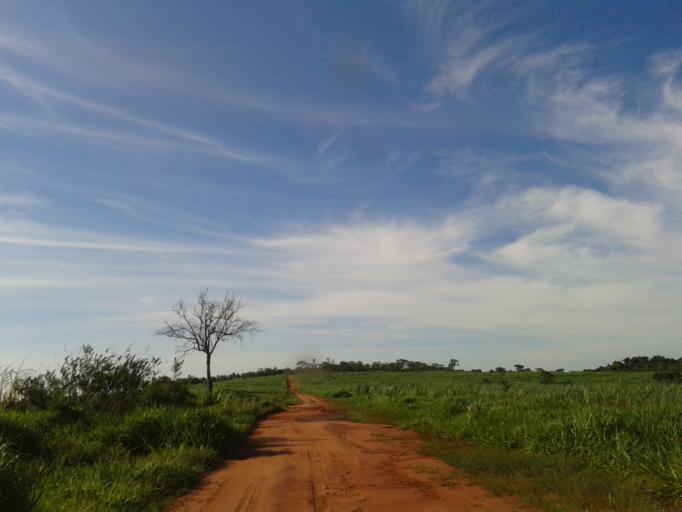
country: BR
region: Minas Gerais
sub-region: Santa Vitoria
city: Santa Vitoria
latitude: -19.1100
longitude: -49.9891
